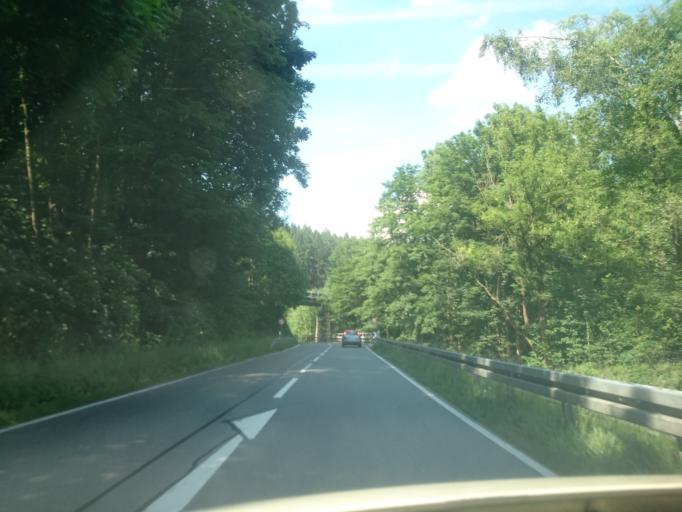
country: DE
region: Saxony
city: Zoblitz
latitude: 50.6585
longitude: 13.2109
